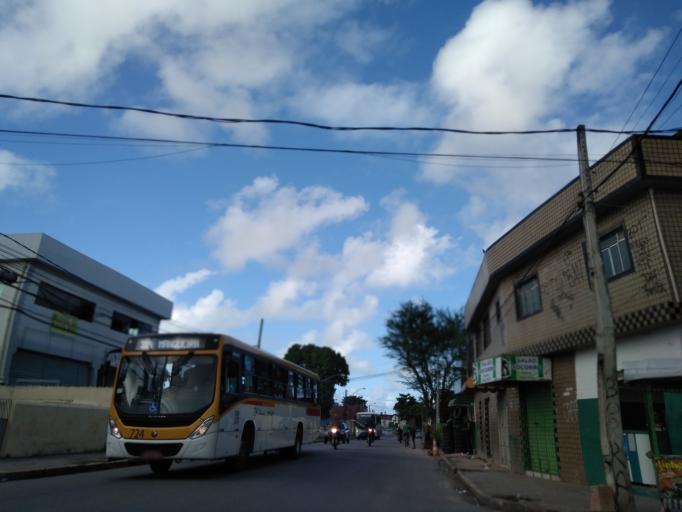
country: BR
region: Pernambuco
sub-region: Recife
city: Recife
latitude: -8.0745
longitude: -34.9218
